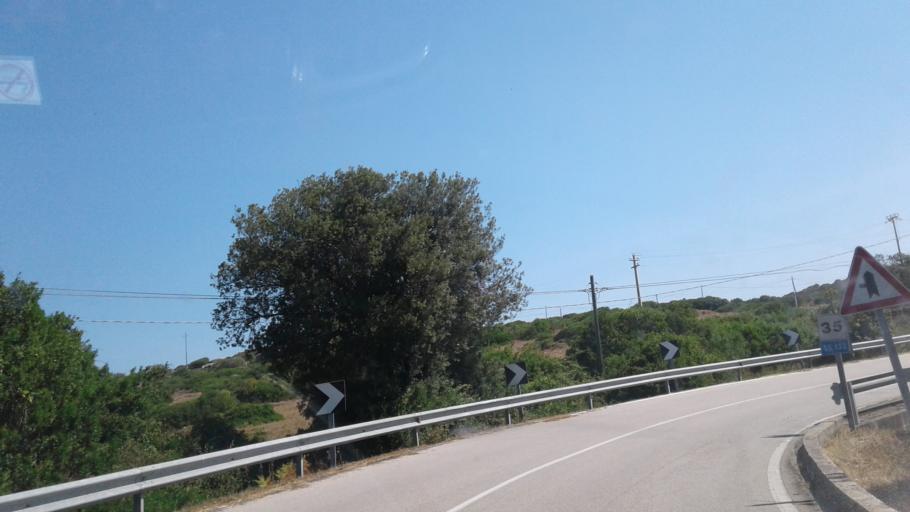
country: IT
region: Sardinia
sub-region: Provincia di Olbia-Tempio
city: Palau
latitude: 41.1287
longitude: 9.2853
